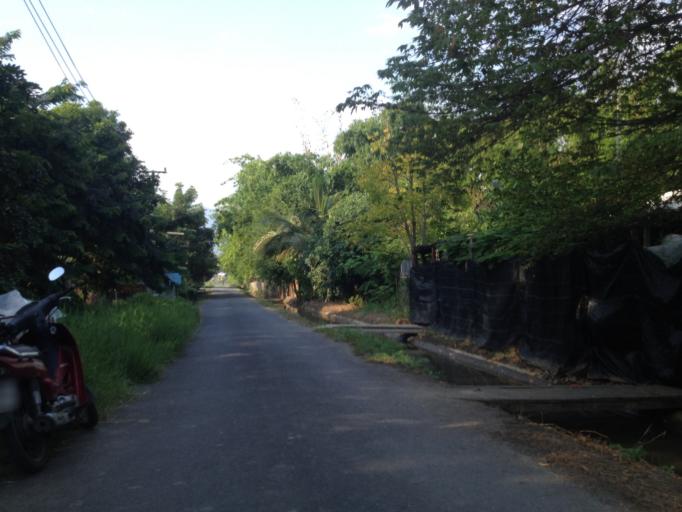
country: TH
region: Chiang Mai
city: Hang Dong
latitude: 18.7296
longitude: 98.9294
